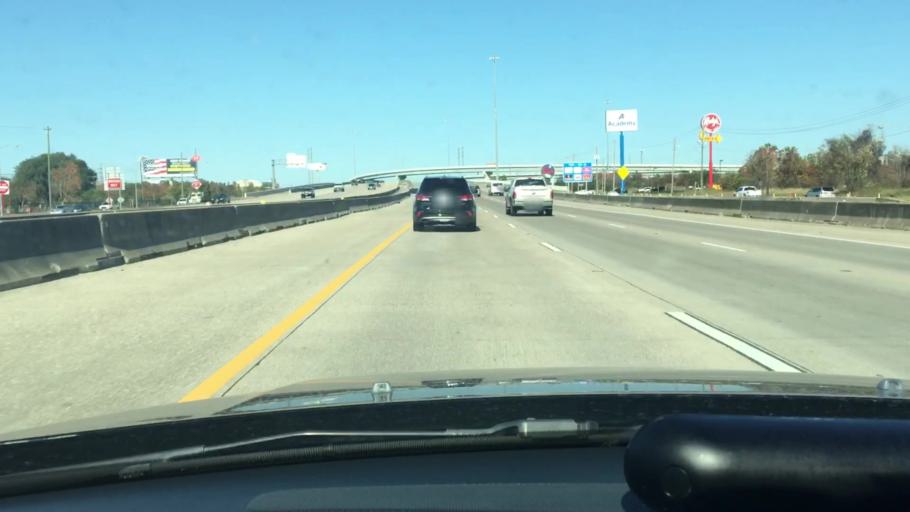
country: US
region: Texas
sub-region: Harris County
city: Webster
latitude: 29.5173
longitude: -95.1225
